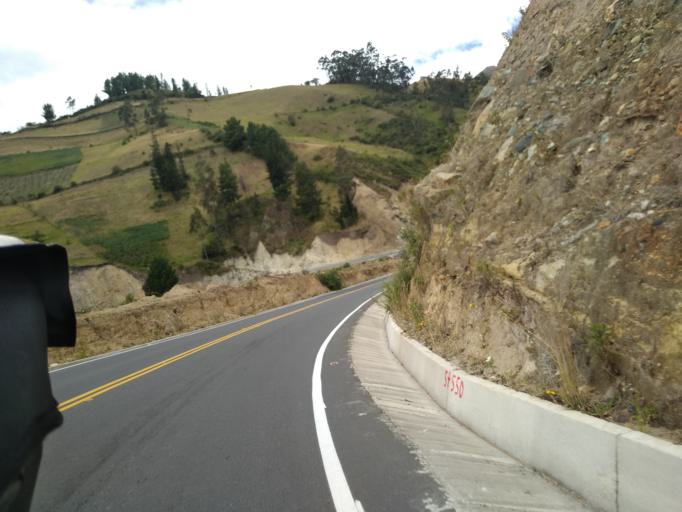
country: EC
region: Cotopaxi
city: Saquisili
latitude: -0.7279
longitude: -78.8996
